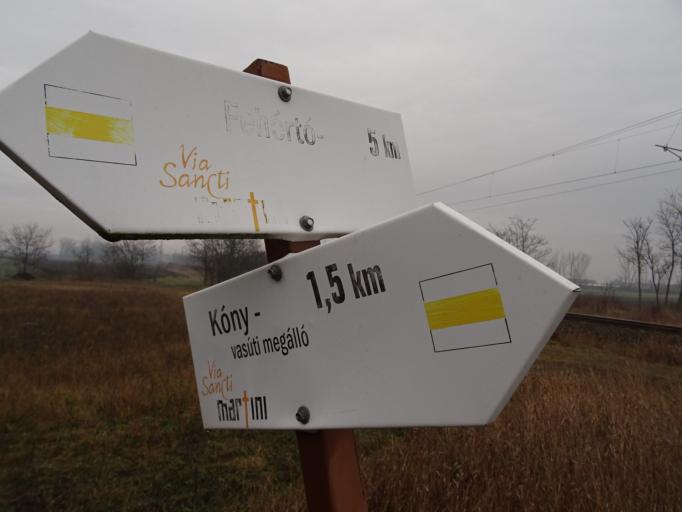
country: HU
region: Gyor-Moson-Sopron
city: Kony
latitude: 47.6369
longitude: 17.3747
